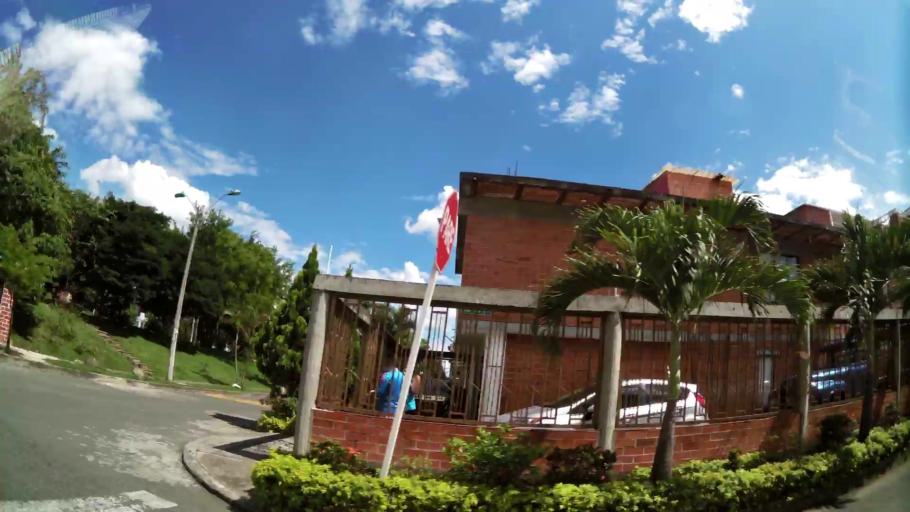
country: CO
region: Valle del Cauca
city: Cali
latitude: 3.3954
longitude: -76.5168
